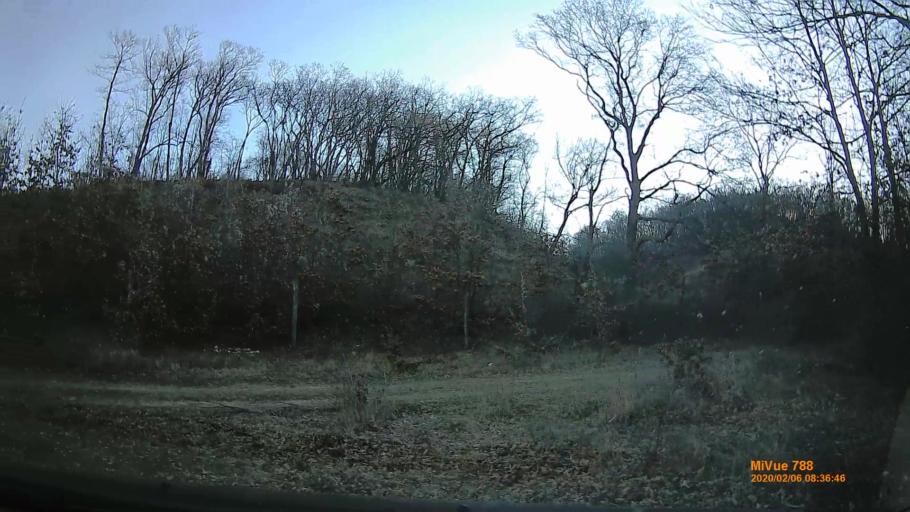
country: HU
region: Fejer
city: Szarliget
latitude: 47.5289
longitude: 18.4969
